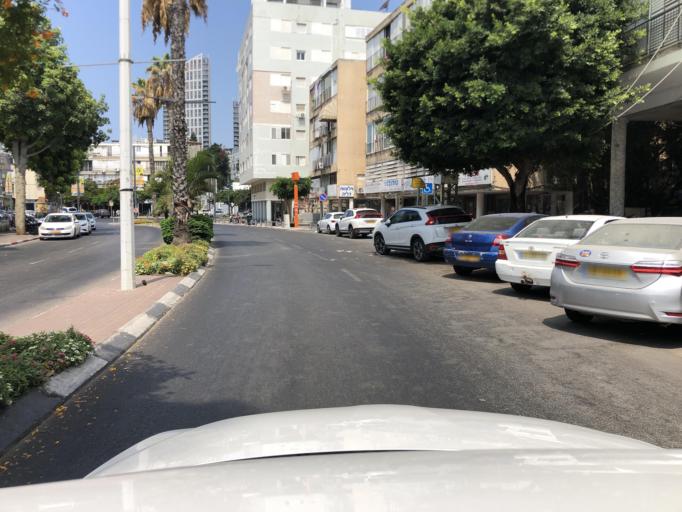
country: IL
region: Tel Aviv
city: Giv`atayim
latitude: 32.0769
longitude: 34.8154
